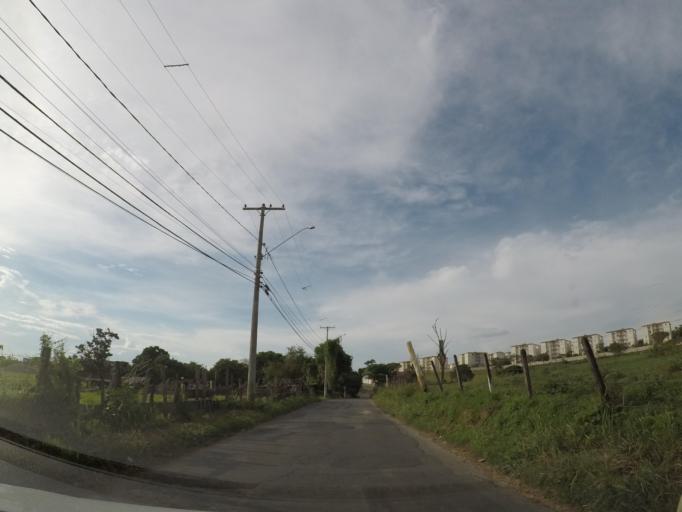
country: BR
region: Sao Paulo
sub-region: Sumare
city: Sumare
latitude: -22.8236
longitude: -47.2486
